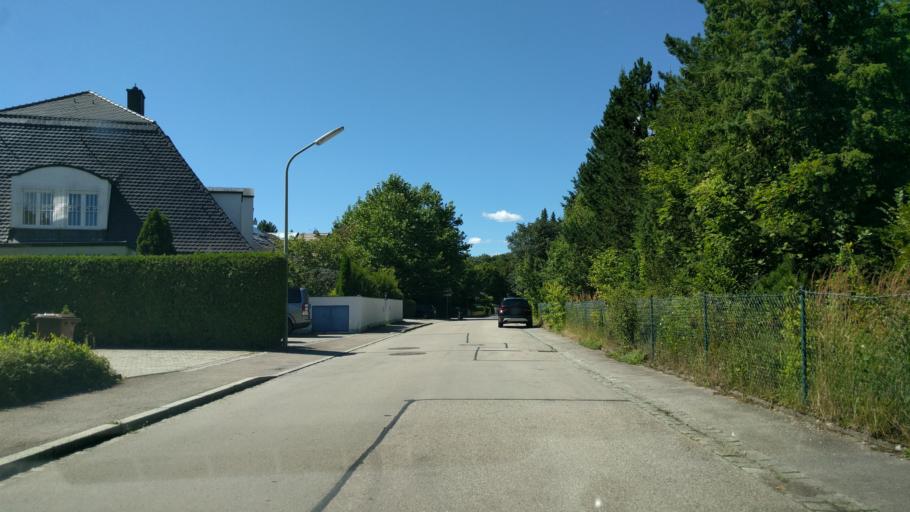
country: DE
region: Bavaria
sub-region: Upper Bavaria
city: Grunwald
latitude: 48.0475
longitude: 11.5271
